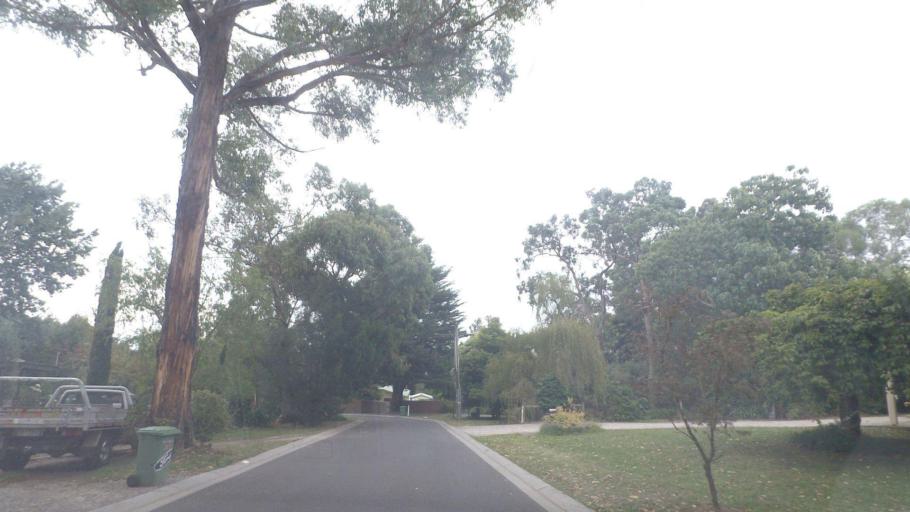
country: AU
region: Victoria
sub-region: Yarra Ranges
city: Mount Evelyn
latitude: -37.7663
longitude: 145.3744
